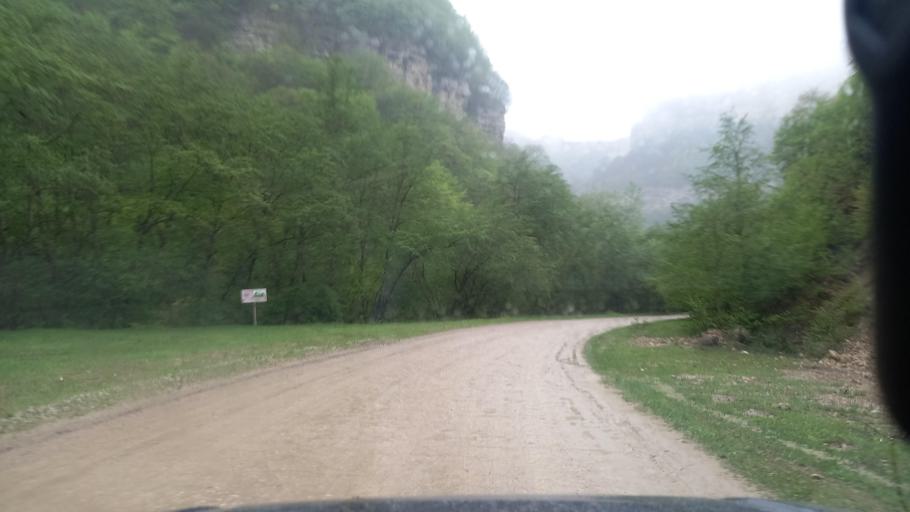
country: RU
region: Kabardino-Balkariya
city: Gundelen
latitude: 43.5909
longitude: 43.1290
